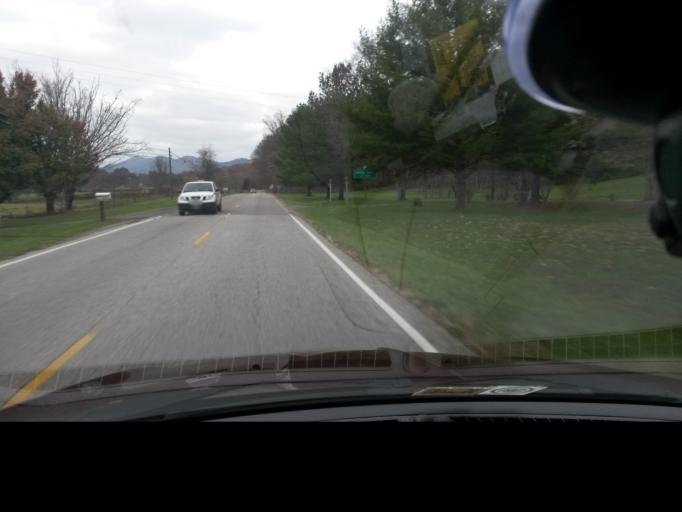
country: US
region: Virginia
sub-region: City of Buena Vista
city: Buena Vista
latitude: 37.7102
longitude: -79.3727
